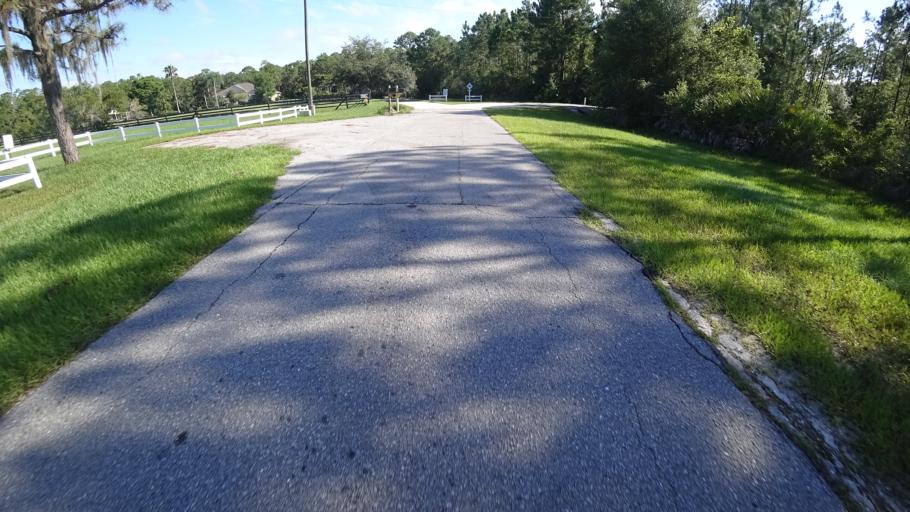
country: US
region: Florida
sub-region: Sarasota County
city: The Meadows
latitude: 27.4185
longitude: -82.3403
